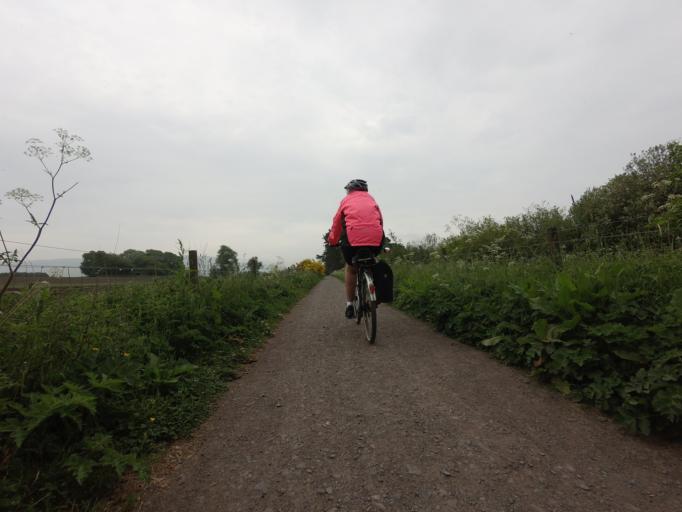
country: GB
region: Scotland
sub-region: Perth and Kinross
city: Milnathort
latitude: 56.2195
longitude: -3.3812
